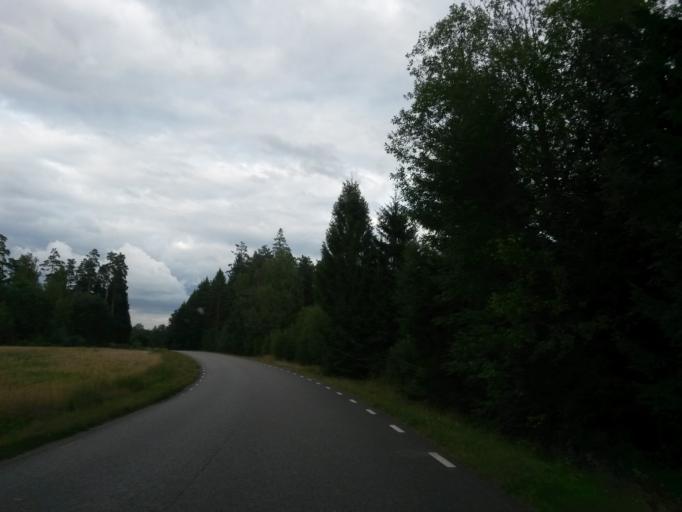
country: SE
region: Vaestra Goetaland
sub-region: Vargarda Kommun
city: Jonstorp
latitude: 57.9829
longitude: 12.7316
